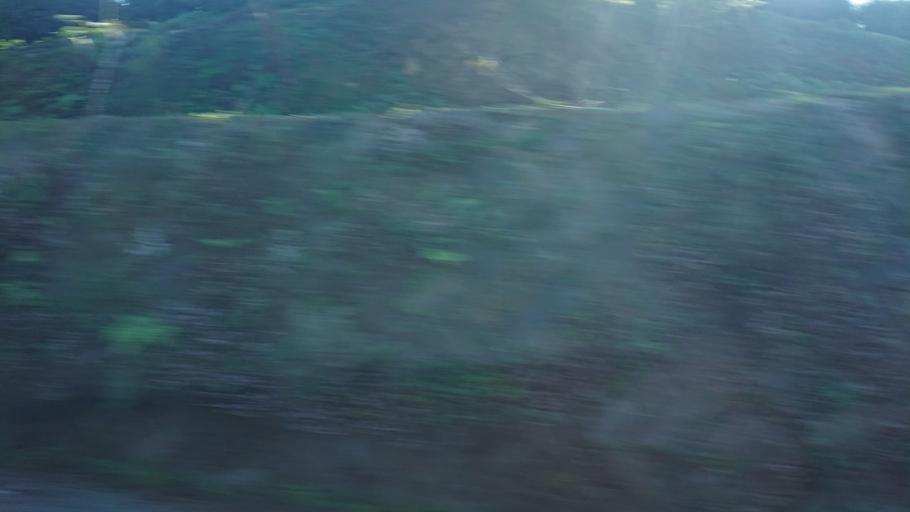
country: TW
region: Taiwan
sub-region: Chiayi
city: Jiayi Shi
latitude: 23.4788
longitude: 120.6986
